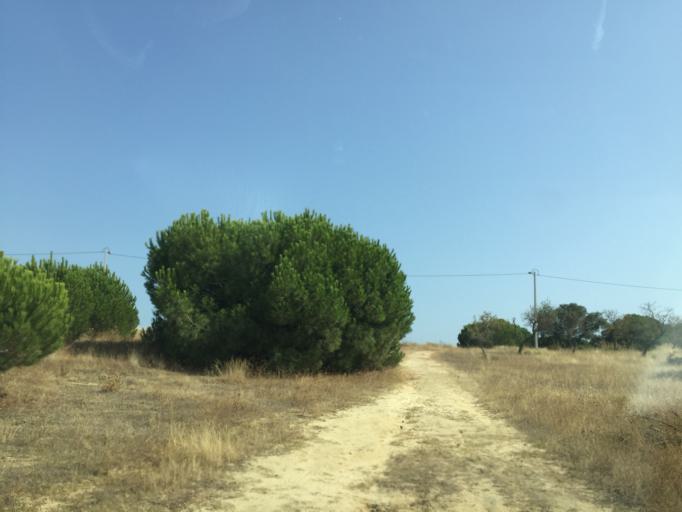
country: PT
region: Faro
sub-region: Albufeira
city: Ferreiras
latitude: 37.0963
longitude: -8.1985
